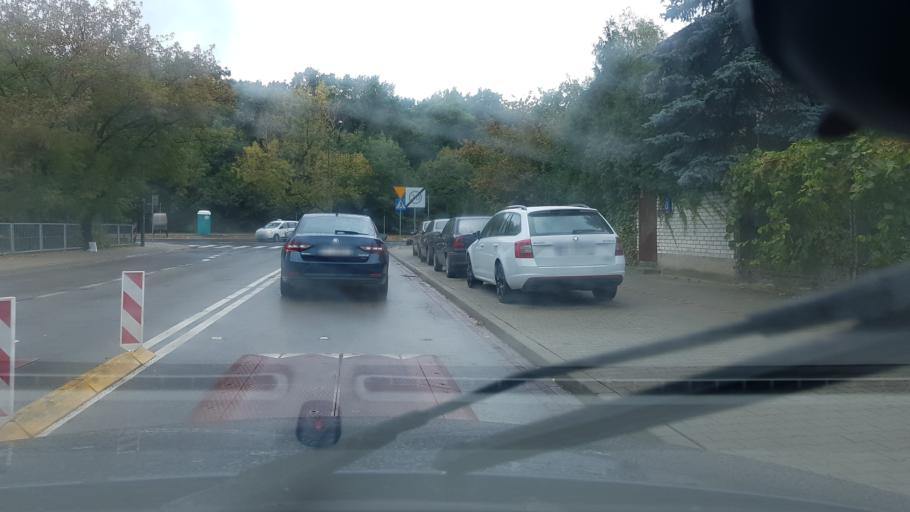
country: PL
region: Masovian Voivodeship
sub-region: Warszawa
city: Zoliborz
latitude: 52.2848
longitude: 20.9709
